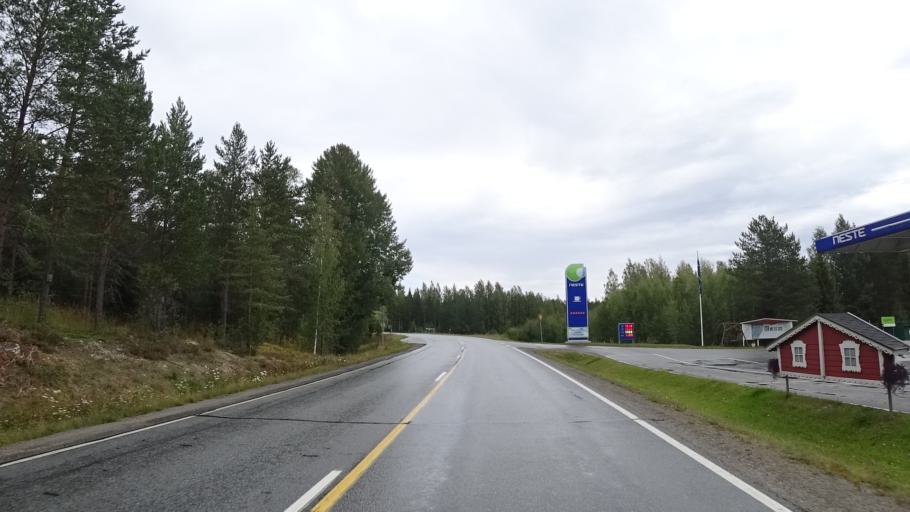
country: FI
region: North Karelia
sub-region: Keski-Karjala
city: Raeaekkylae
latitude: 62.0544
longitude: 29.6123
